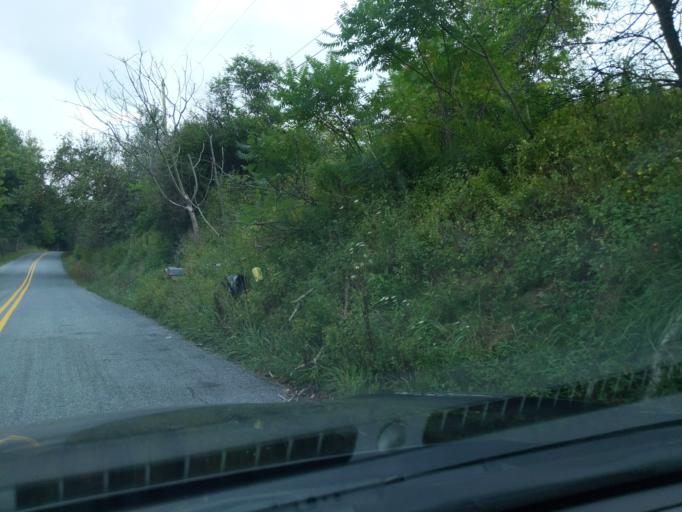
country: US
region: Pennsylvania
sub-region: Cambria County
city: Portage
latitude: 40.3420
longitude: -78.5846
